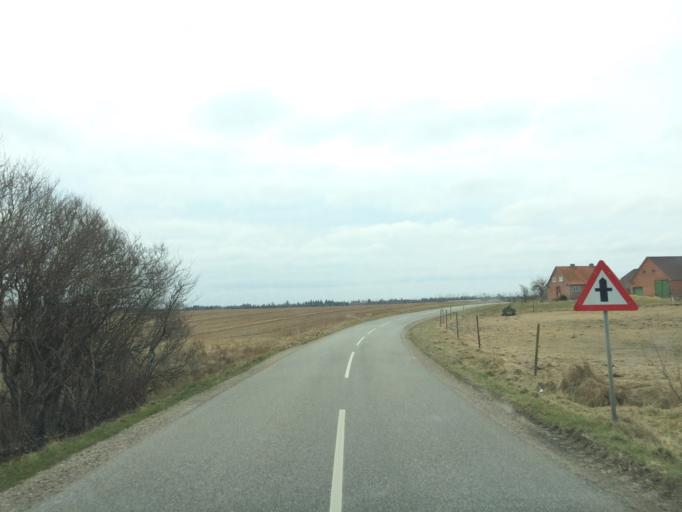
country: DK
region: Central Jutland
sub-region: Ringkobing-Skjern Kommune
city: Tarm
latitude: 55.8122
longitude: 8.3940
